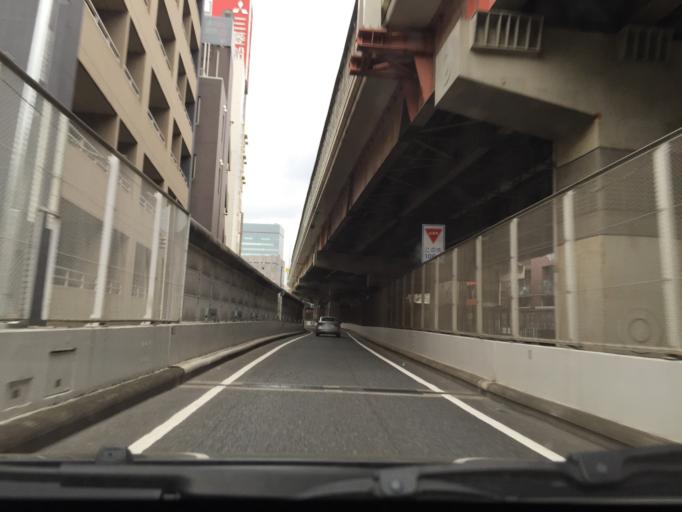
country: JP
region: Tokyo
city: Tokyo
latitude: 35.6836
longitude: 139.7900
